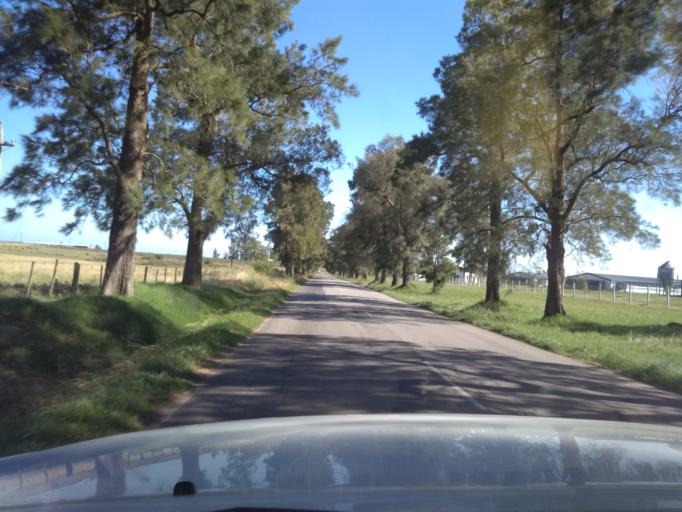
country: UY
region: Canelones
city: San Bautista
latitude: -34.3925
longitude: -55.9596
